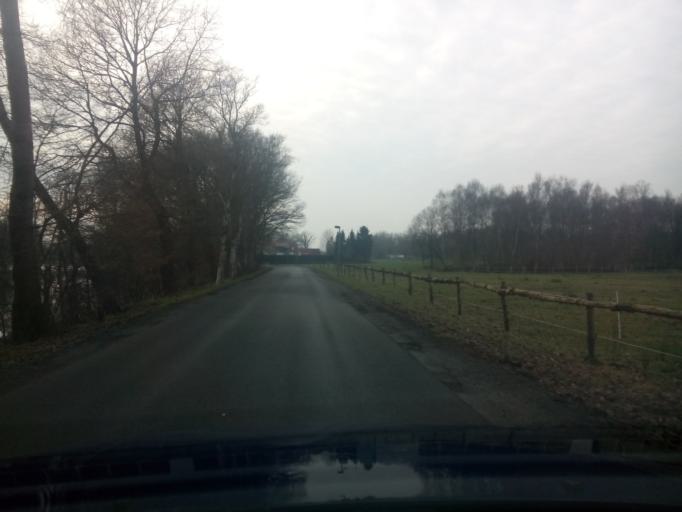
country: DE
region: Lower Saxony
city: Lilienthal
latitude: 53.1428
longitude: 8.9616
